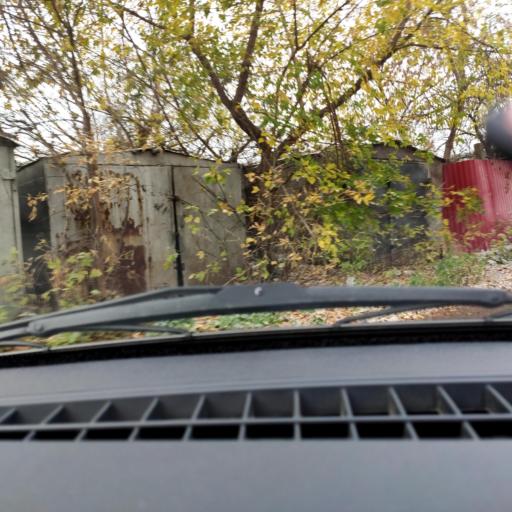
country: RU
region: Bashkortostan
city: Ufa
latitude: 54.8001
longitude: 56.0367
